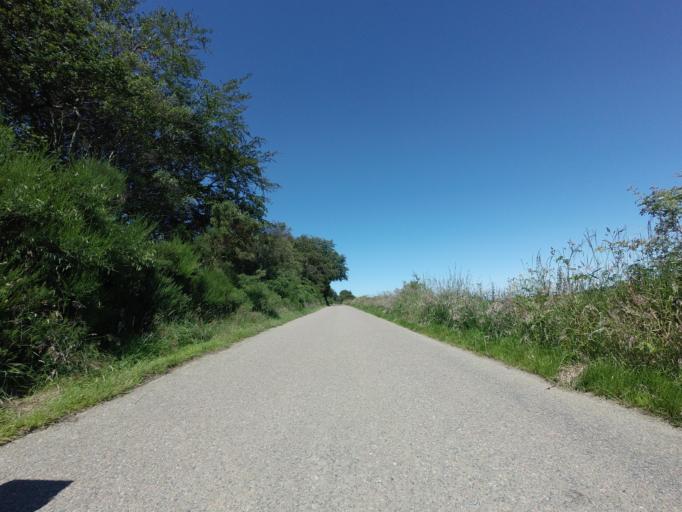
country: GB
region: Scotland
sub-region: Aberdeenshire
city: Macduff
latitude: 57.6477
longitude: -2.5044
